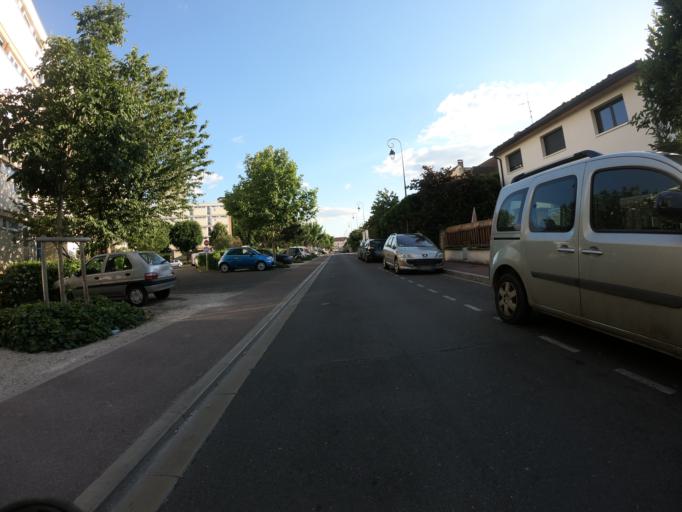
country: FR
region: Ile-de-France
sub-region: Departement du Val-de-Marne
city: Fresnes
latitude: 48.7588
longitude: 2.3120
